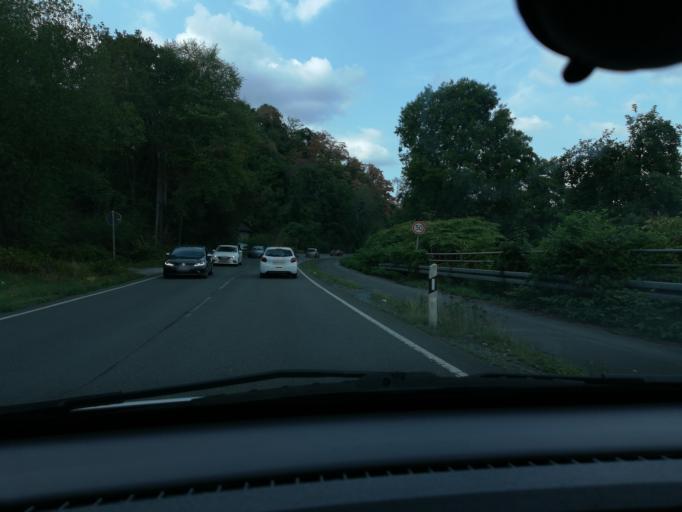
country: DE
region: North Rhine-Westphalia
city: Witten
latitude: 51.4266
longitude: 7.3018
